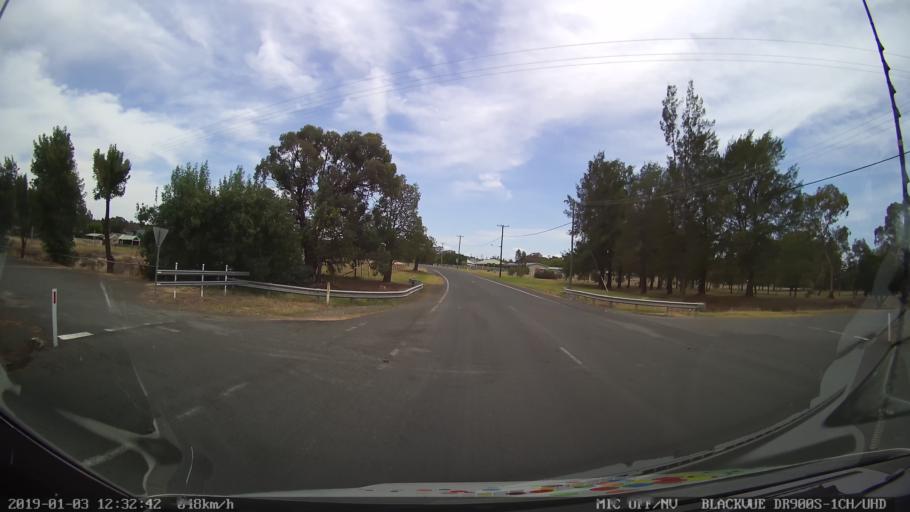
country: AU
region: New South Wales
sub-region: Weddin
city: Grenfell
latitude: -33.8915
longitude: 148.1619
